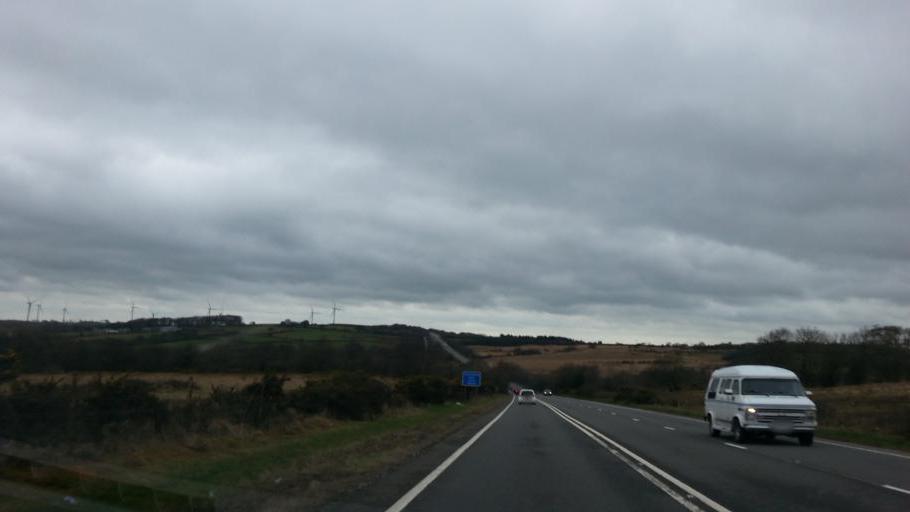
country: GB
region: England
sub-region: Devon
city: Tiverton
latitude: 50.9798
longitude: -3.6453
